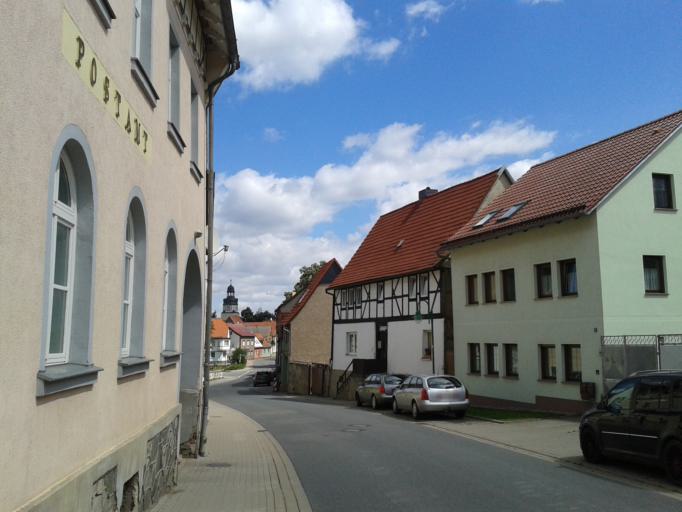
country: DE
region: Saxony-Anhalt
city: Wippra
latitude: 51.5719
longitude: 11.2720
